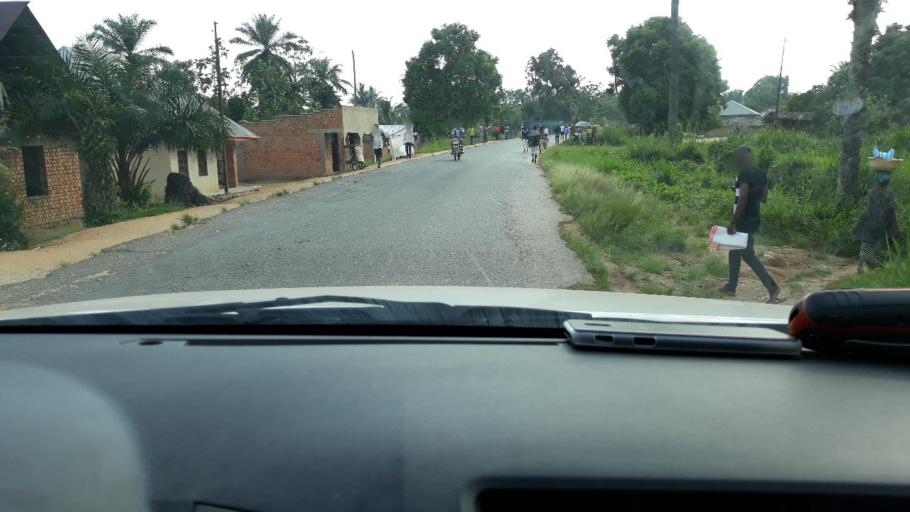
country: CD
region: Maniema
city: Kindu
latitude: -2.9531
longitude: 25.9397
